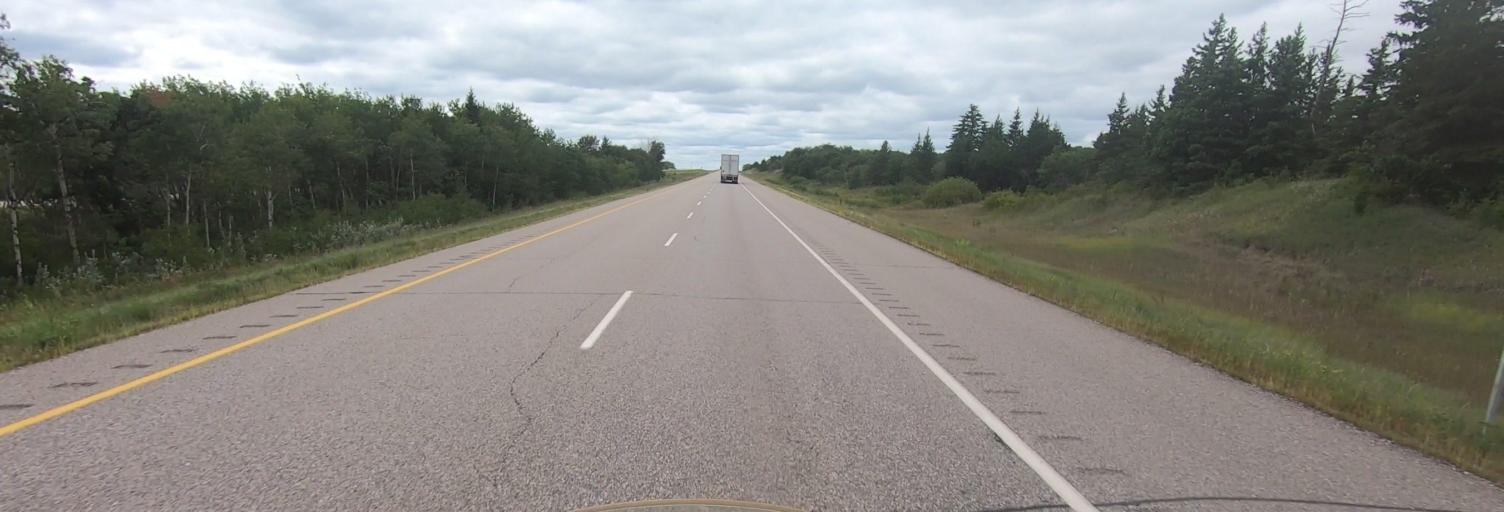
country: CA
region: Manitoba
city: Carberry
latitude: 49.9015
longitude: -99.2650
